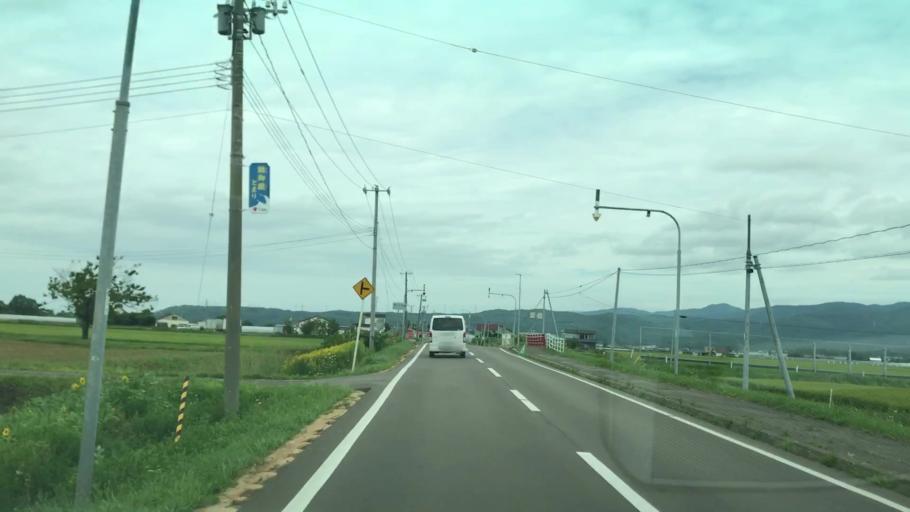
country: JP
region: Hokkaido
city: Iwanai
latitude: 43.0092
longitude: 140.5780
